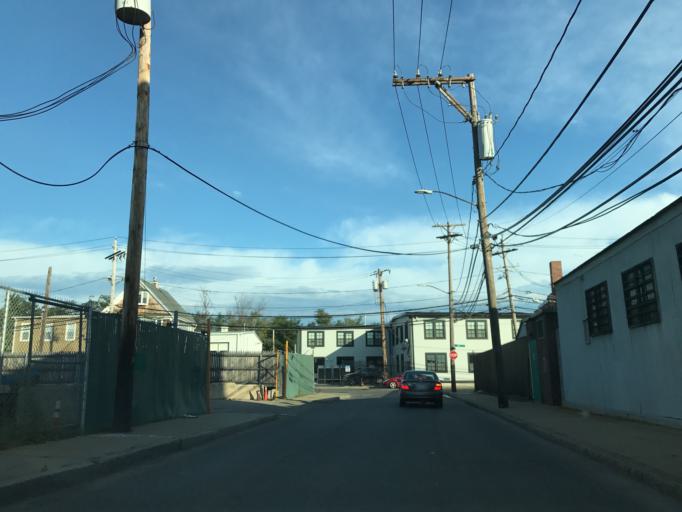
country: US
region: Massachusetts
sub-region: Suffolk County
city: South Boston
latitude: 42.2996
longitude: -71.0561
